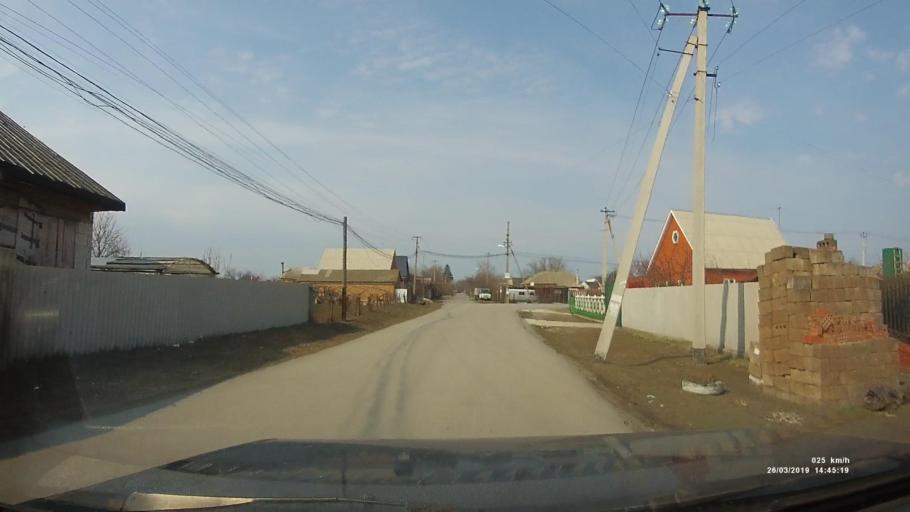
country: RU
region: Rostov
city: Novobessergenovka
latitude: 47.1819
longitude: 38.8619
